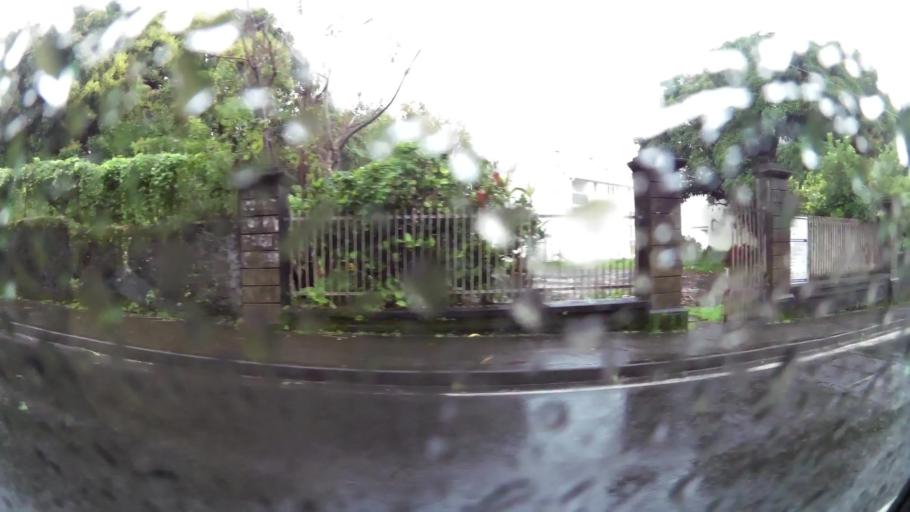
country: RE
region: Reunion
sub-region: Reunion
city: Saint-Benoit
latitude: -21.0318
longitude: 55.7116
